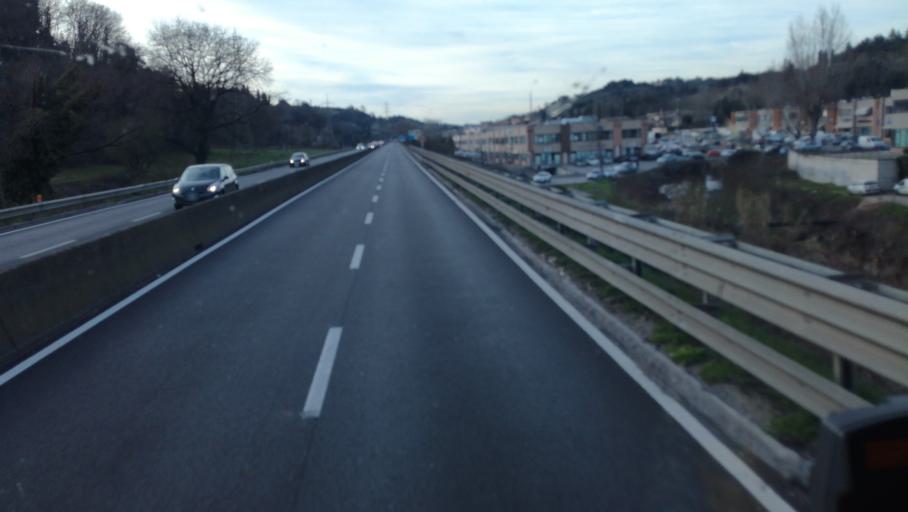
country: IT
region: Tuscany
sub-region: Provincia di Siena
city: Siena
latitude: 43.3019
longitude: 11.3231
